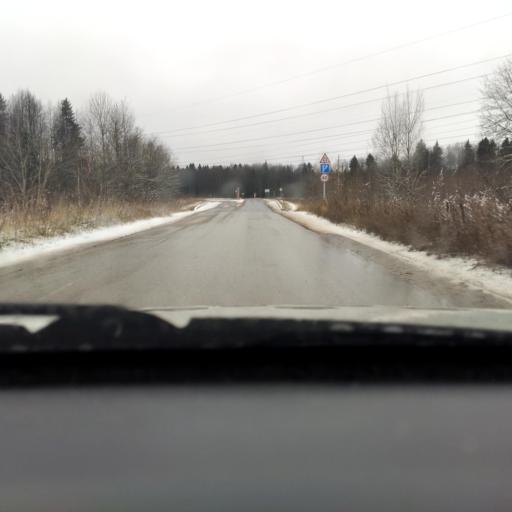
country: RU
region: Perm
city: Ferma
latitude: 57.9751
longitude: 56.3486
